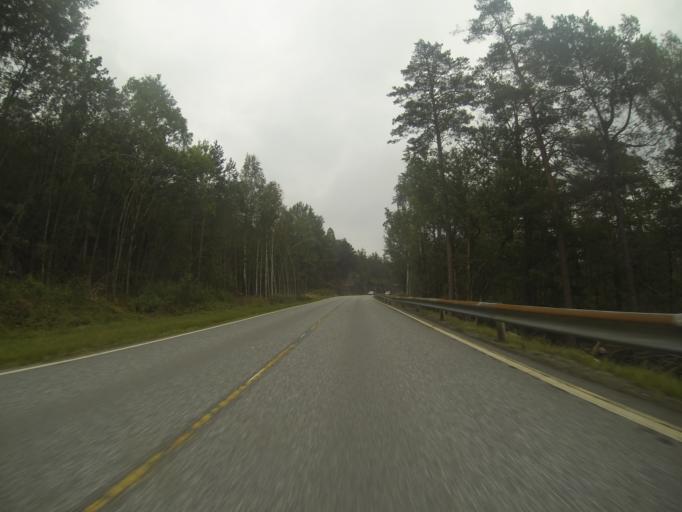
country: NO
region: Rogaland
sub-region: Suldal
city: Sand
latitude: 59.5184
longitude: 6.2345
